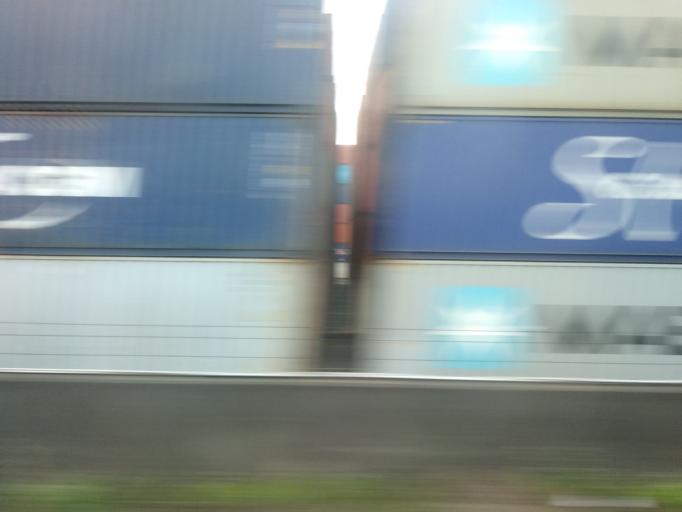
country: TW
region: Taiwan
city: Daxi
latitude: 24.9148
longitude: 121.1783
